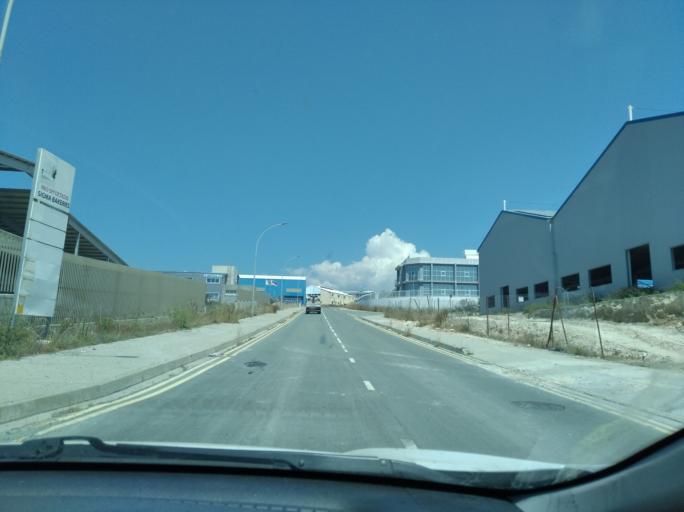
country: CY
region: Limassol
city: Ypsonas
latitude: 34.7271
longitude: 32.9438
